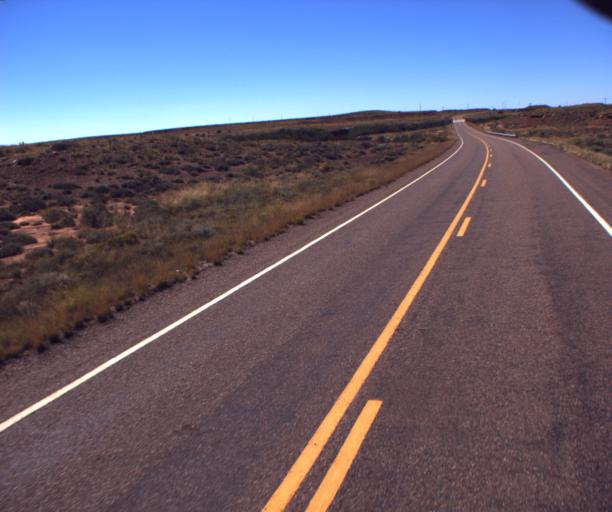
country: US
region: Arizona
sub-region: Navajo County
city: Holbrook
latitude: 34.8840
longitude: -110.1033
